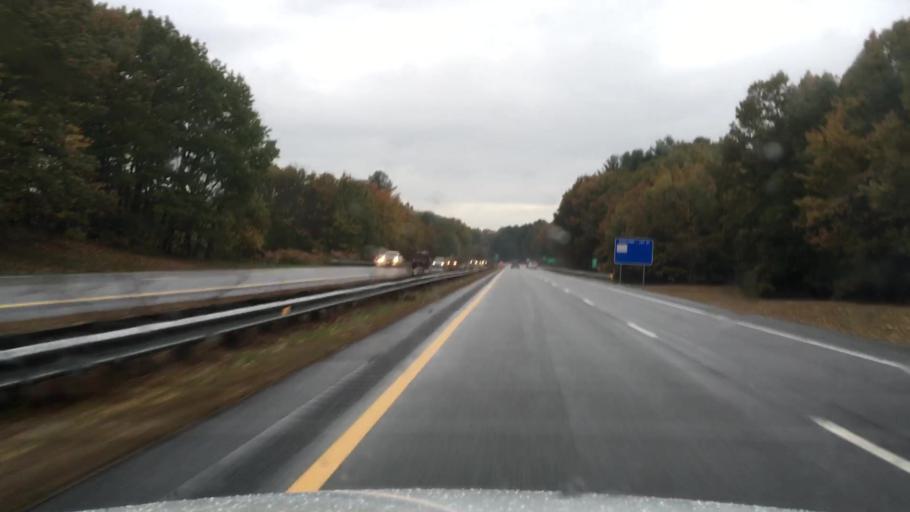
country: US
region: New Hampshire
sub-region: Strafford County
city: Dover
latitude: 43.1685
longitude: -70.8592
